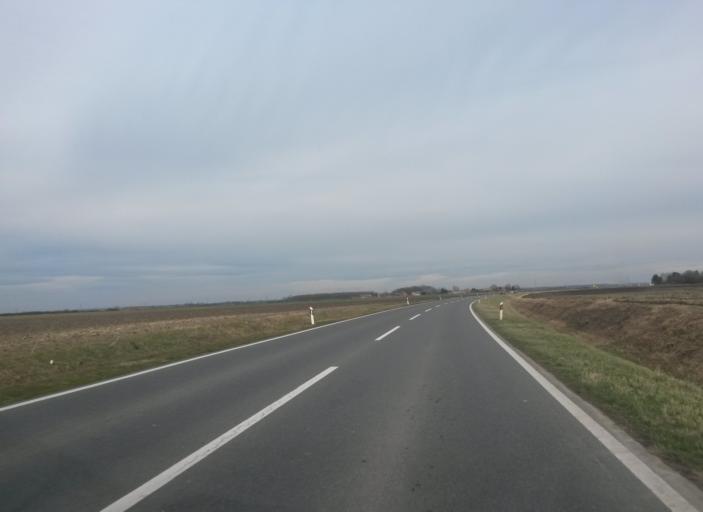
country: HR
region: Osjecko-Baranjska
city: Cepin
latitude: 45.5329
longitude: 18.5502
